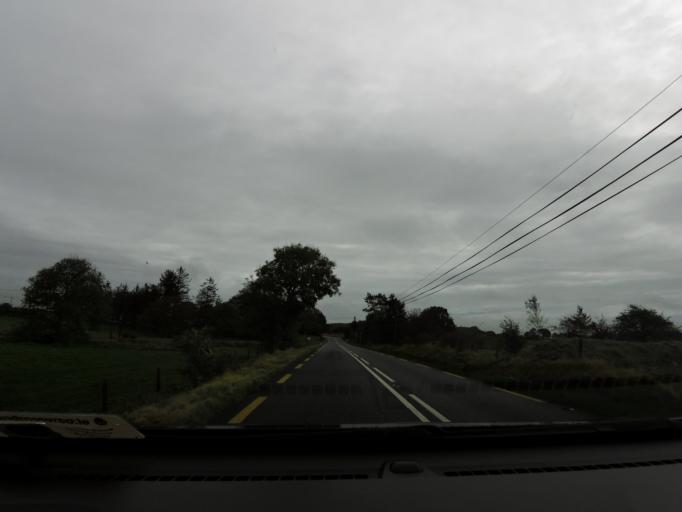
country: IE
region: Connaught
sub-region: County Galway
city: Tuam
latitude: 53.6034
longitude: -8.7582
